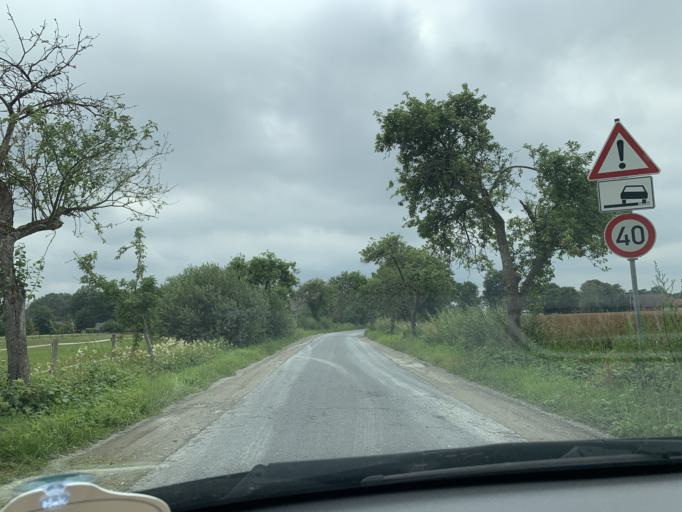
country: DE
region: North Rhine-Westphalia
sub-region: Regierungsbezirk Munster
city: Ennigerloh
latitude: 51.8334
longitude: 8.0737
